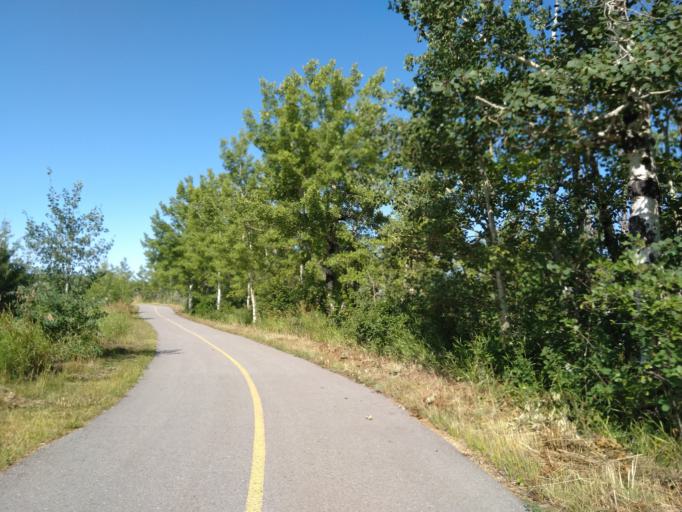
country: CA
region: Alberta
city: Calgary
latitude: 51.0968
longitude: -114.2462
